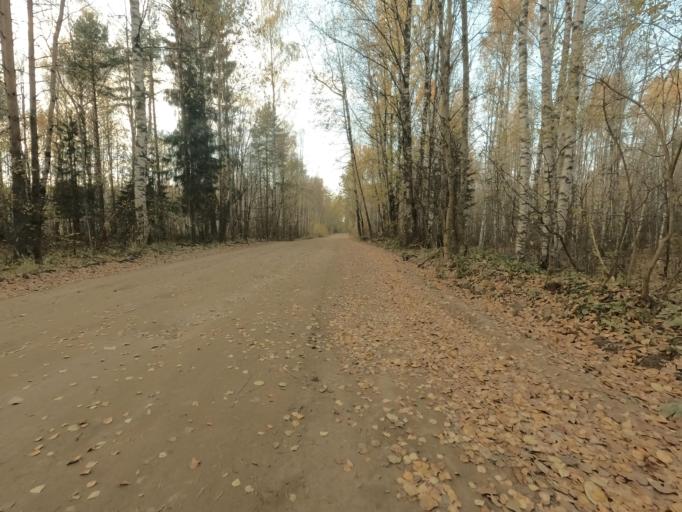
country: RU
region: Leningrad
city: Priladozhskiy
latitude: 59.7440
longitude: 31.3108
